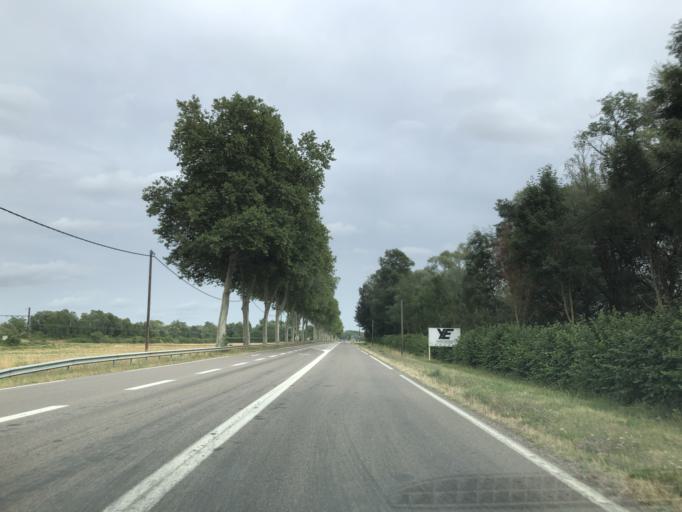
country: FR
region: Bourgogne
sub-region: Departement de l'Yonne
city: Joigny
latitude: 47.9636
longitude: 3.4310
